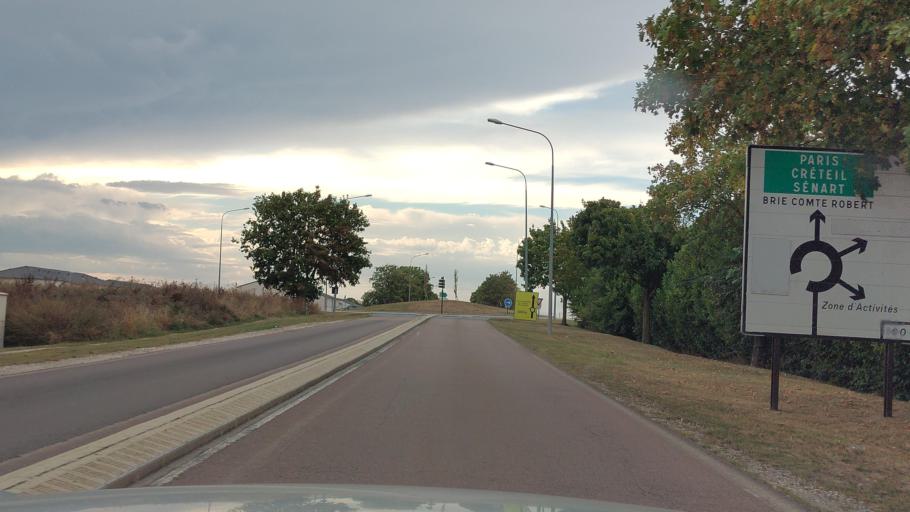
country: FR
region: Ile-de-France
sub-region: Departement de Seine-et-Marne
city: Mormant
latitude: 48.6132
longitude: 2.8809
